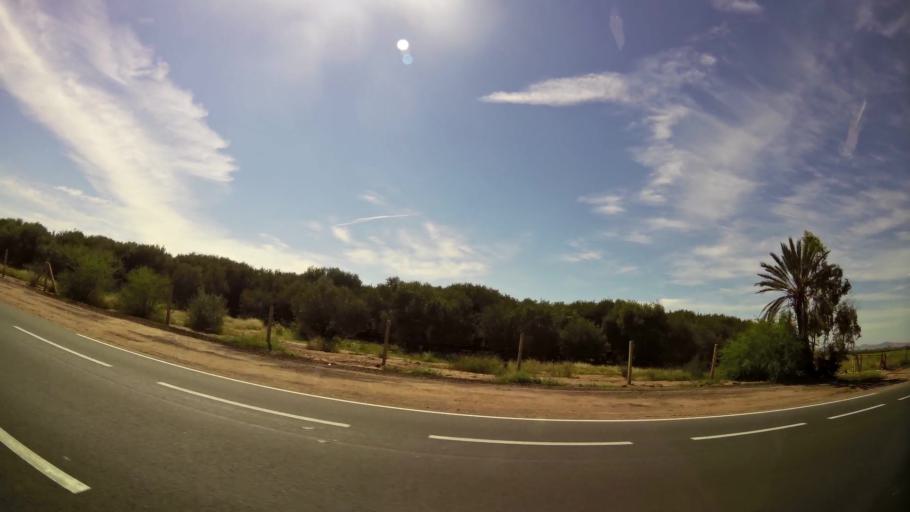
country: MA
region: Marrakech-Tensift-Al Haouz
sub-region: Marrakech
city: Marrakesh
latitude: 31.6516
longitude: -8.1053
